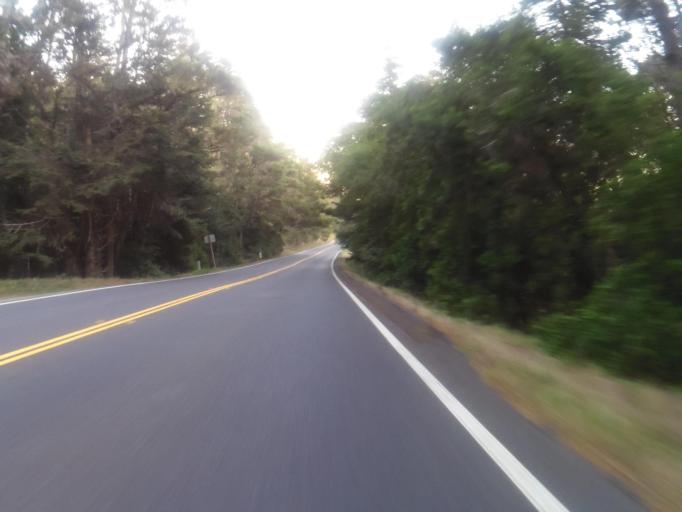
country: US
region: California
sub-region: Sonoma County
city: Sea Ranch
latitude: 38.6055
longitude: -123.3602
